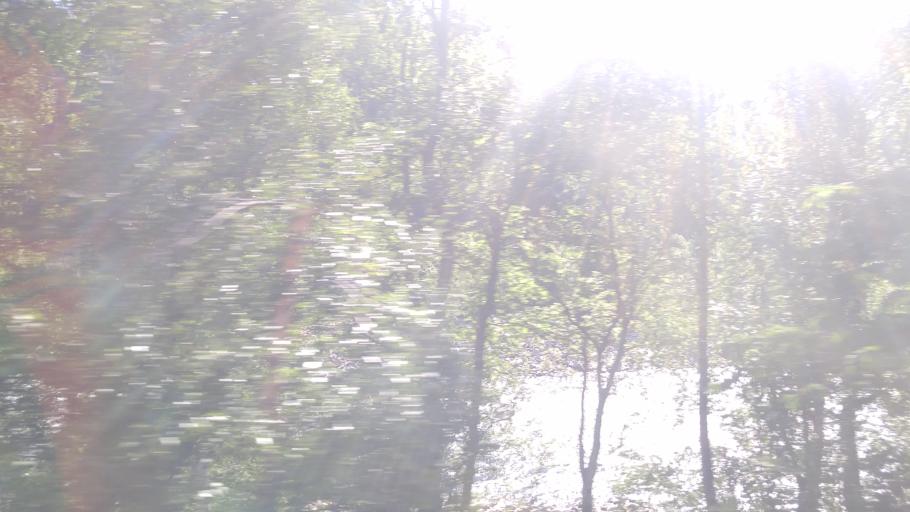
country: NO
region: Sor-Trondelag
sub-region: Midtre Gauldal
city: Storen
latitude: 63.0022
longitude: 10.4618
